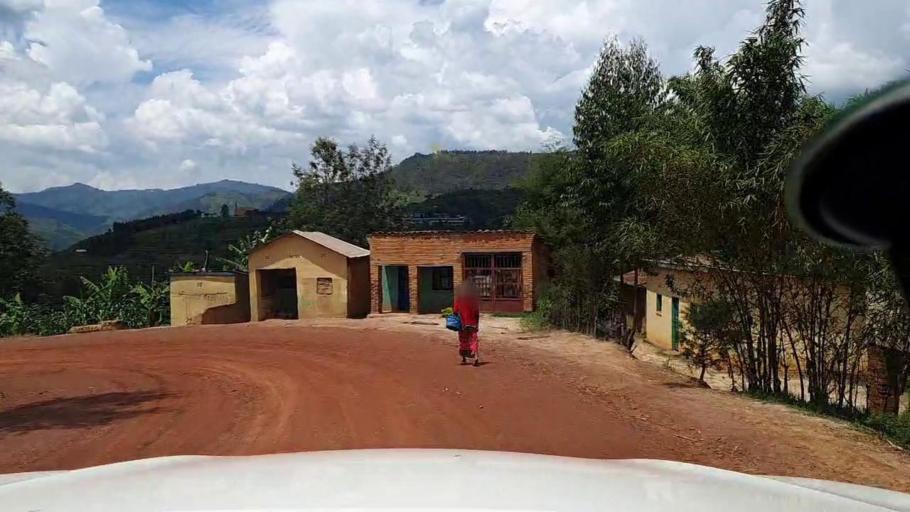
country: RW
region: Northern Province
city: Byumba
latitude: -1.6898
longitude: 29.8250
